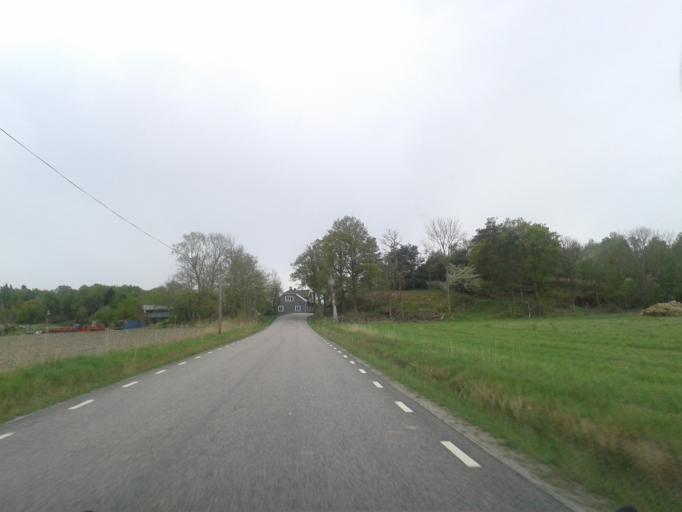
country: SE
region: Vaestra Goetaland
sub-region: Stenungsunds Kommun
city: Stora Hoga
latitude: 57.9739
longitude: 11.8286
